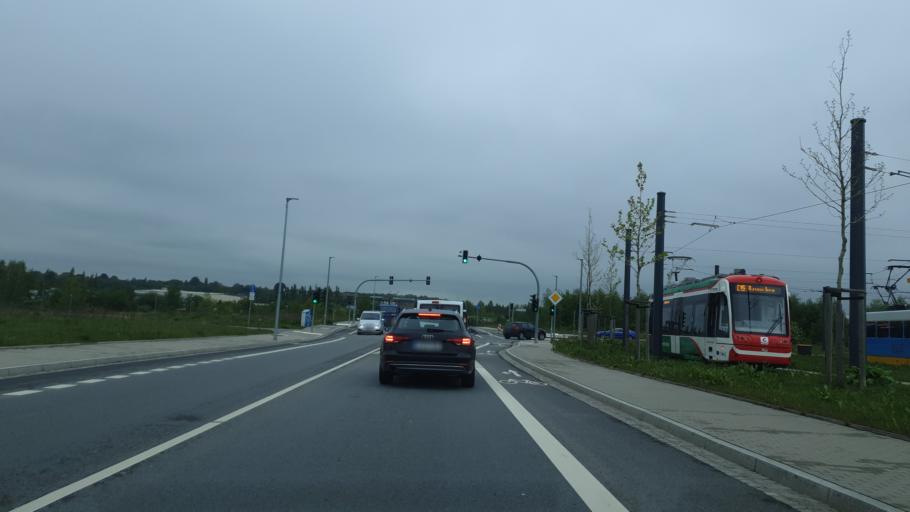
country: DE
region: Saxony
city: Chemnitz
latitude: 50.8106
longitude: 12.9231
